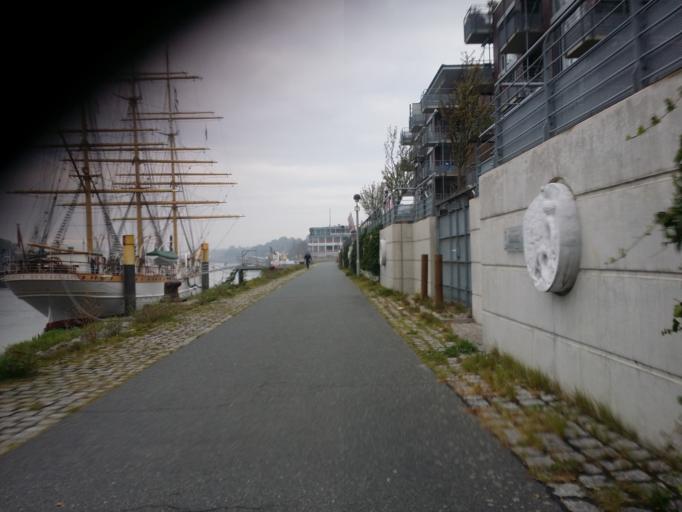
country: DE
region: Lower Saxony
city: Lemwerder
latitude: 53.1659
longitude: 8.6277
